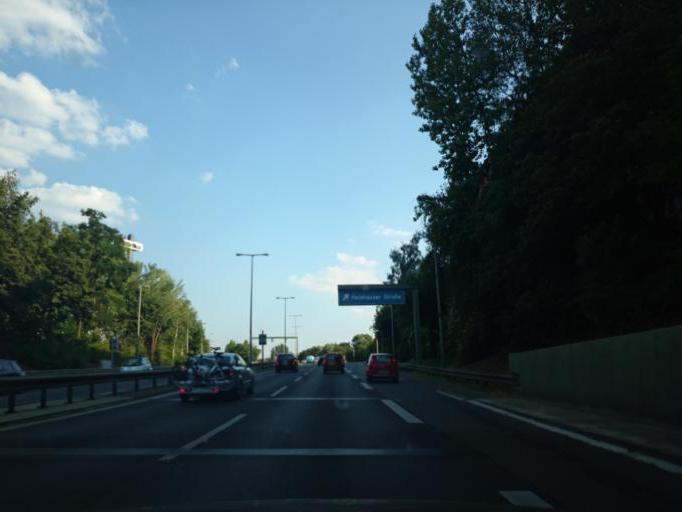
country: DE
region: Berlin
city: Tegel
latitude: 52.5802
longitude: 13.2956
